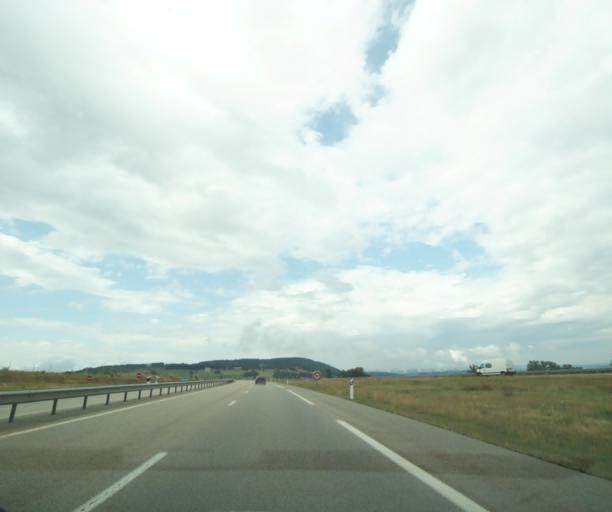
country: FR
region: Auvergne
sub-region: Departement de la Haute-Loire
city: Yssingeaux
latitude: 45.1630
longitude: 4.1328
